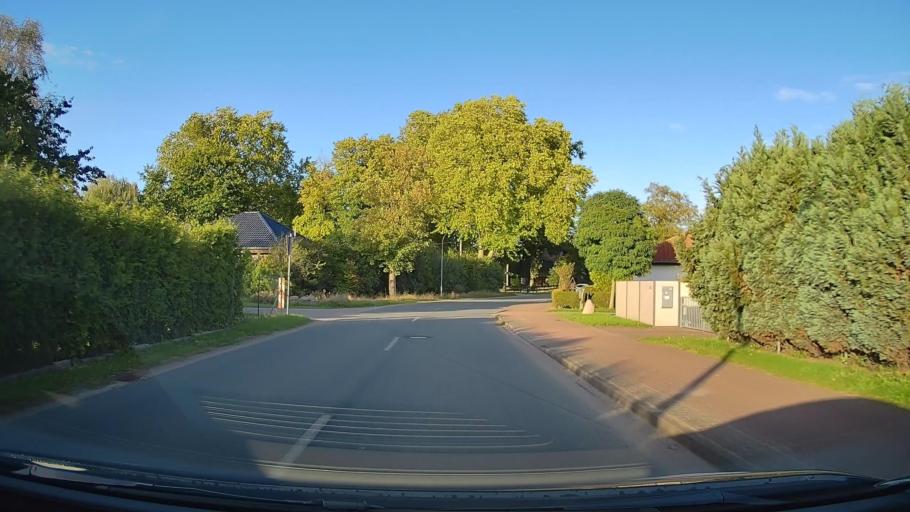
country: DE
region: Mecklenburg-Vorpommern
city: Steinhagen
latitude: 54.1900
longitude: 13.0168
